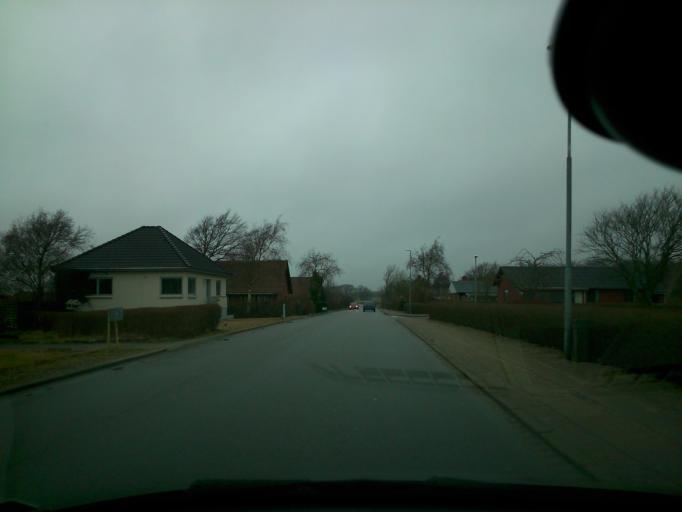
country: DK
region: Central Jutland
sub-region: Ringkobing-Skjern Kommune
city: Ringkobing
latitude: 56.1133
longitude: 8.4225
